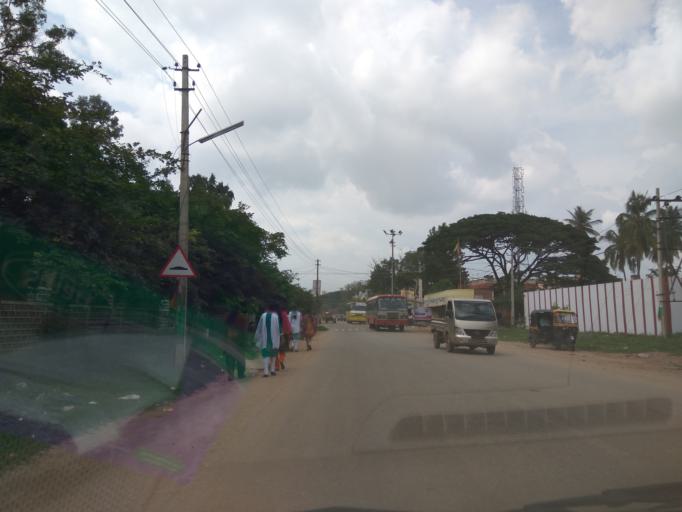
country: IN
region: Karnataka
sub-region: Kolar
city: Kolar
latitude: 13.1314
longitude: 78.1353
